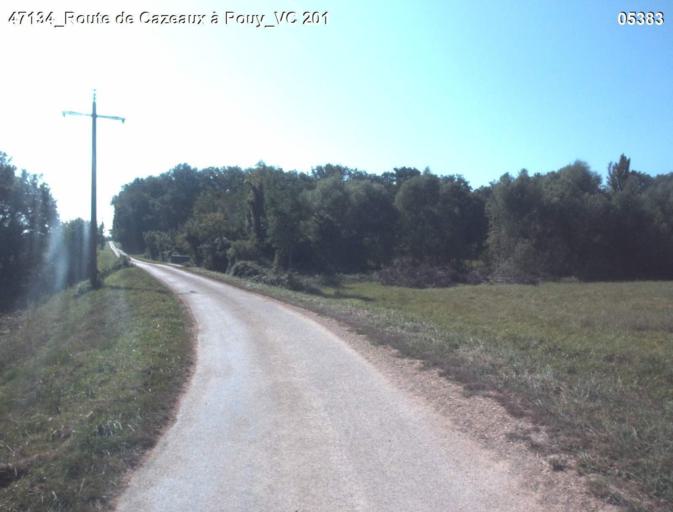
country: FR
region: Aquitaine
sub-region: Departement du Lot-et-Garonne
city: Mezin
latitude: 44.0432
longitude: 0.3090
